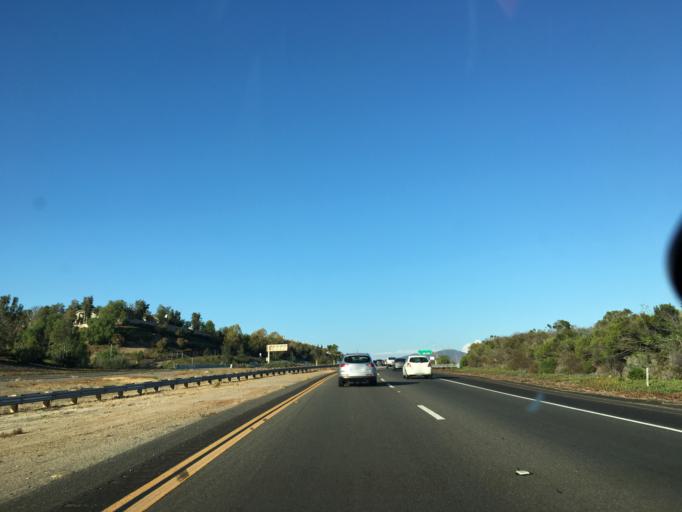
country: US
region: California
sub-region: San Diego County
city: Fairbanks Ranch
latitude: 32.9485
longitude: -117.2039
